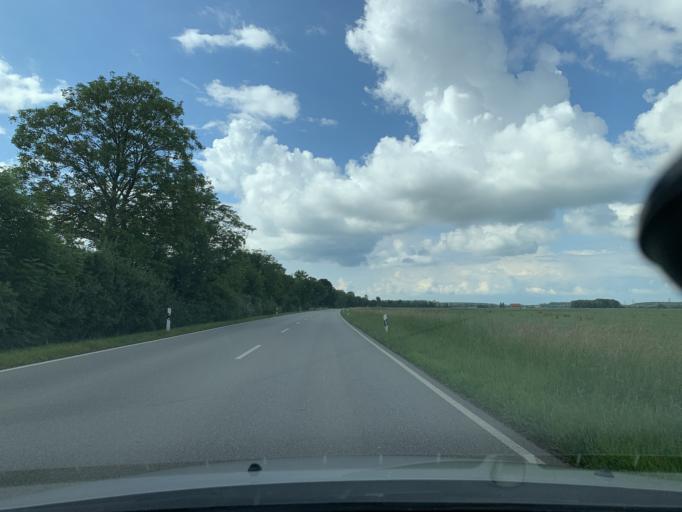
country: DE
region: Bavaria
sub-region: Upper Bavaria
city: Otterfing
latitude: 47.9321
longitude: 11.6547
